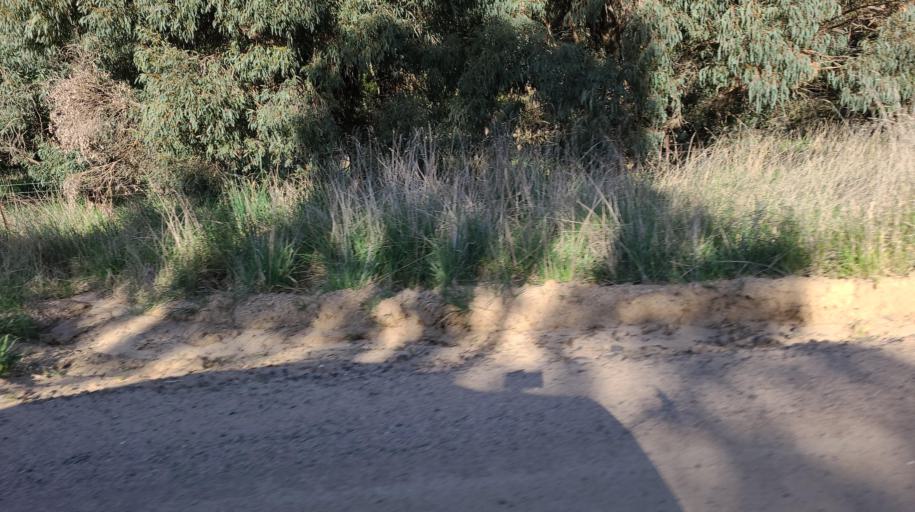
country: AU
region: New South Wales
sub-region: Blayney
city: Millthorpe
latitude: -33.4031
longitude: 149.3080
